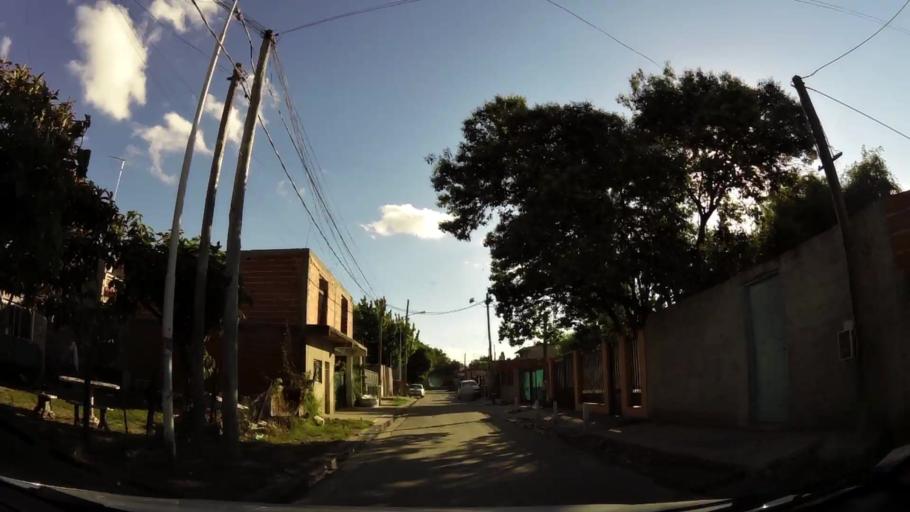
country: AR
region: Buenos Aires
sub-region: Partido de Moron
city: Moron
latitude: -34.6807
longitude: -58.6208
